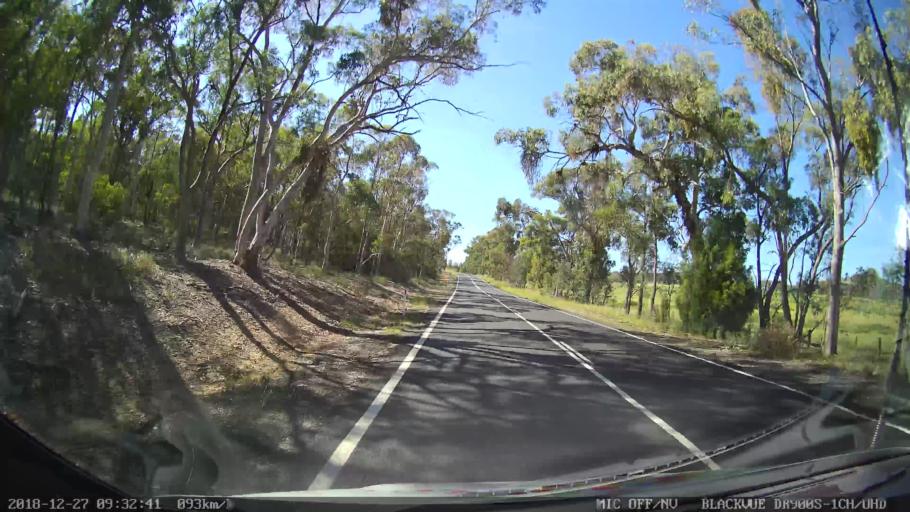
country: AU
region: New South Wales
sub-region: Lithgow
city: Portland
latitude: -33.2106
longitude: 150.0169
